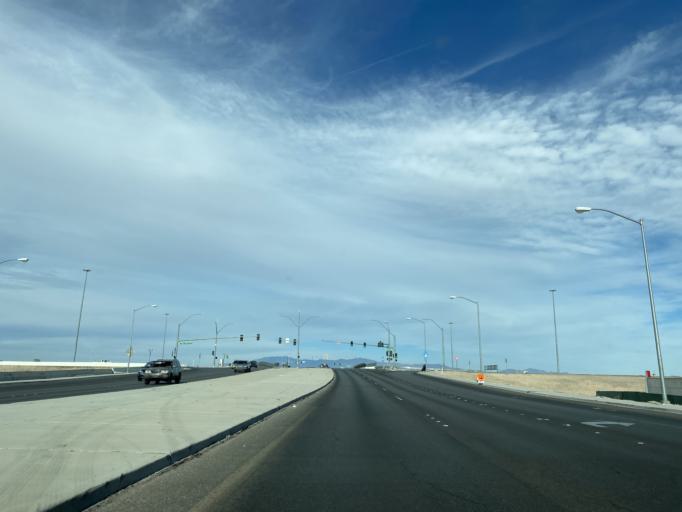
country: US
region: Nevada
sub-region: Clark County
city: Enterprise
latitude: 36.0646
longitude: -115.2245
